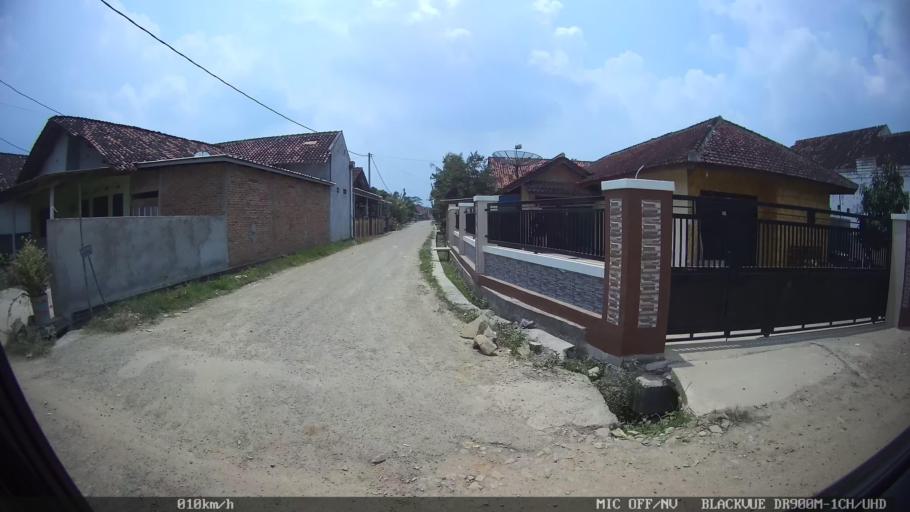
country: ID
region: Lampung
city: Pringsewu
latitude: -5.3655
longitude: 105.0006
